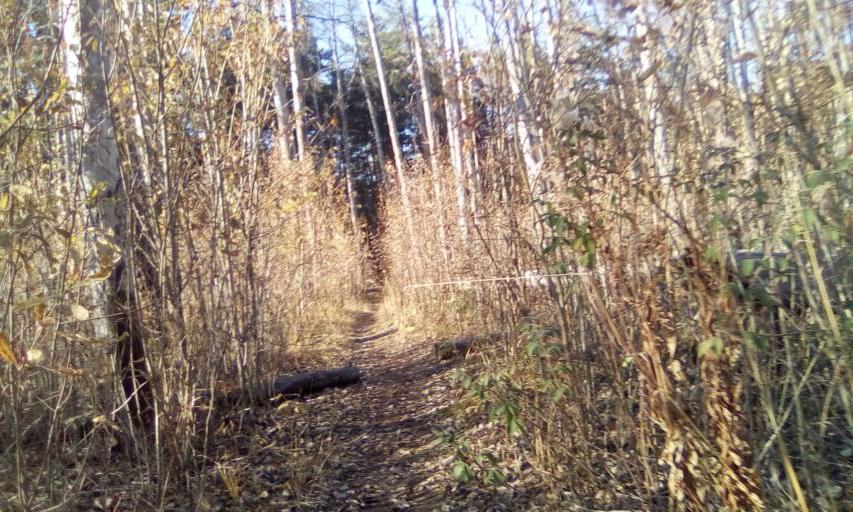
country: RU
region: Chelyabinsk
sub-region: Gorod Chelyabinsk
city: Chelyabinsk
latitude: 55.1629
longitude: 61.3545
